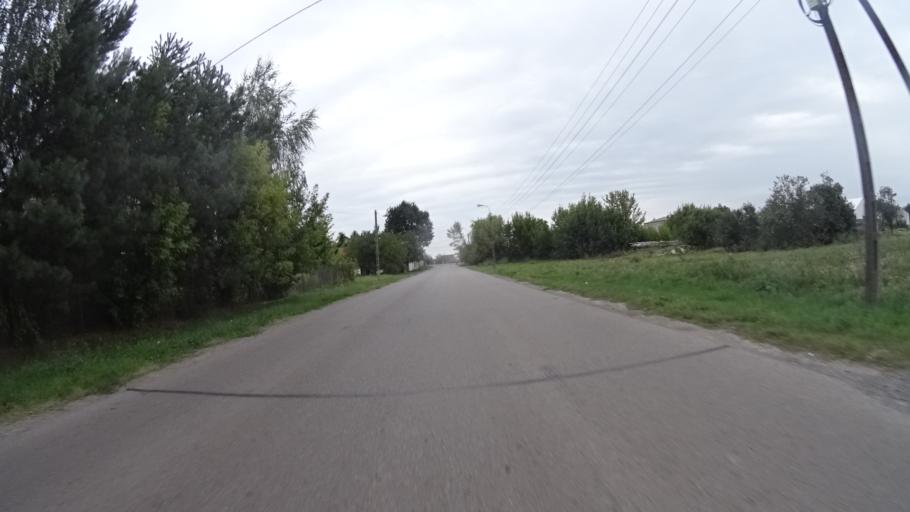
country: PL
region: Masovian Voivodeship
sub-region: Powiat warszawski zachodni
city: Hornowek
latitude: 52.2533
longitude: 20.7909
